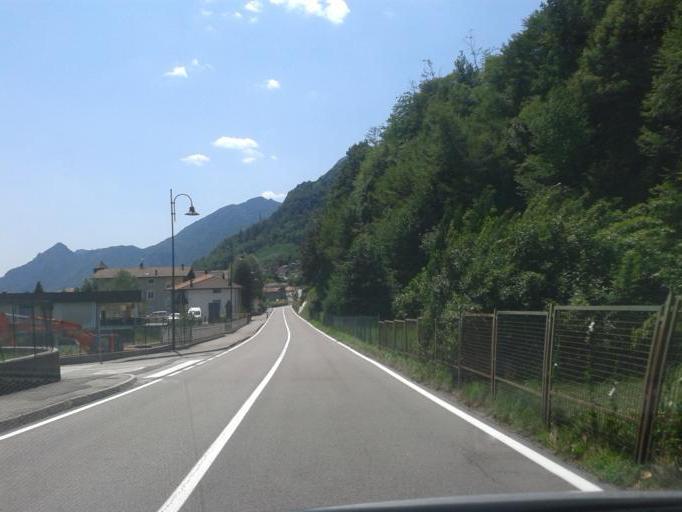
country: IT
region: Trentino-Alto Adige
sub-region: Provincia di Trento
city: Lodrone-Darzo
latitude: 45.8288
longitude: 10.5347
